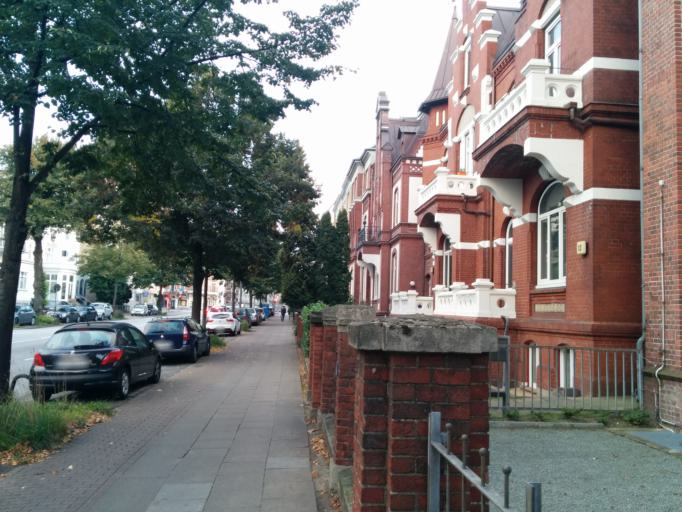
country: DE
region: Hamburg
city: Borgfelde
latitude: 53.5653
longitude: 10.0328
